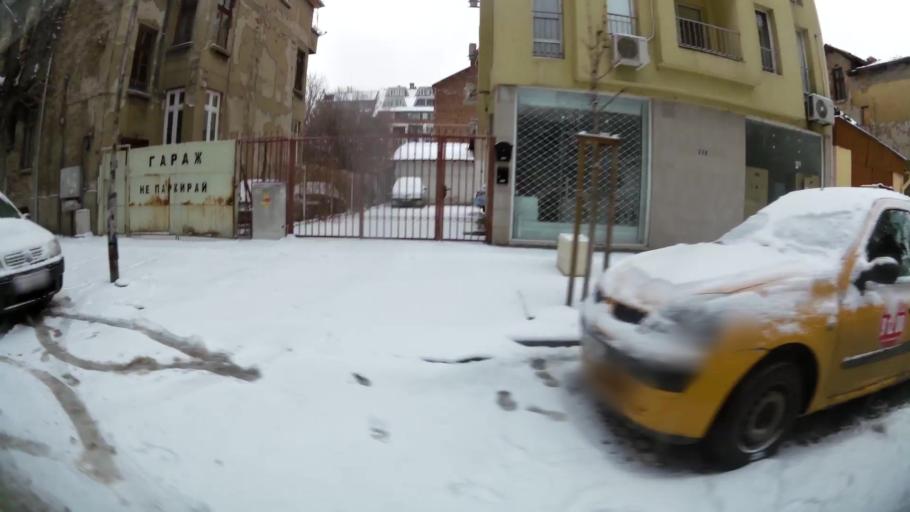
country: BG
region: Sofia-Capital
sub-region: Stolichna Obshtina
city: Sofia
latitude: 42.7043
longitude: 23.3056
